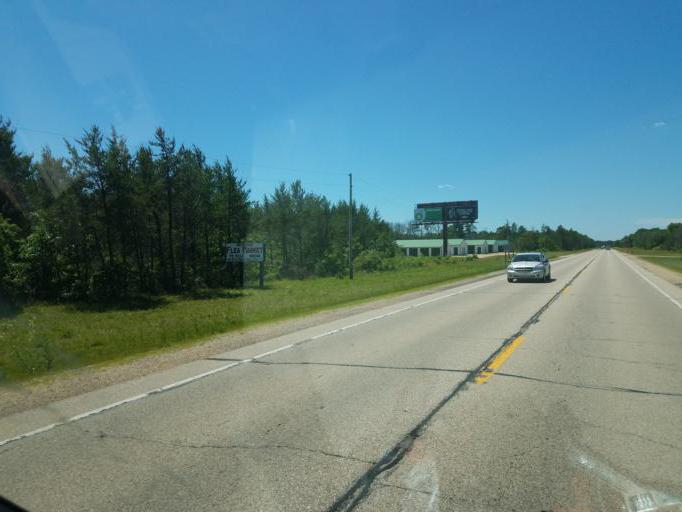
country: US
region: Wisconsin
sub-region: Juneau County
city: New Lisbon
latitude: 44.0374
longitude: -90.0368
